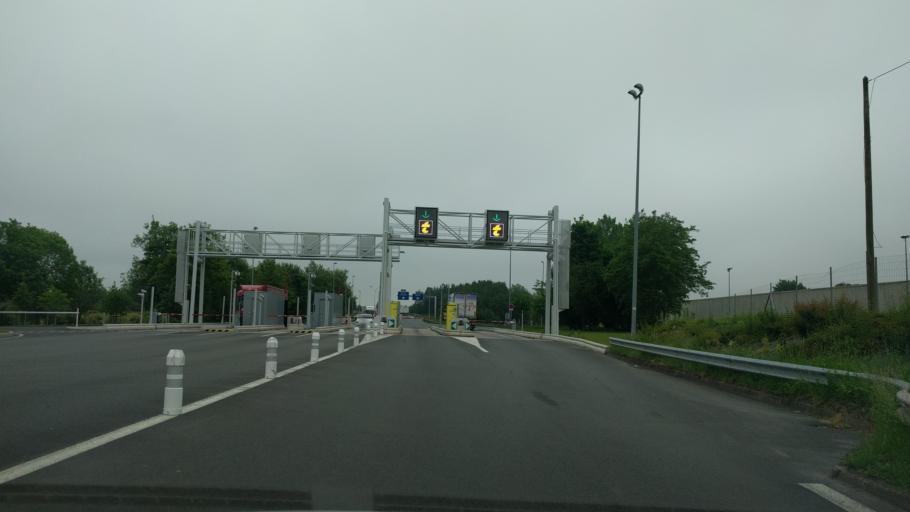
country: FR
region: Nord-Pas-de-Calais
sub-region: Departement du Pas-de-Calais
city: Bapaume
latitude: 50.1047
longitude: 2.8674
